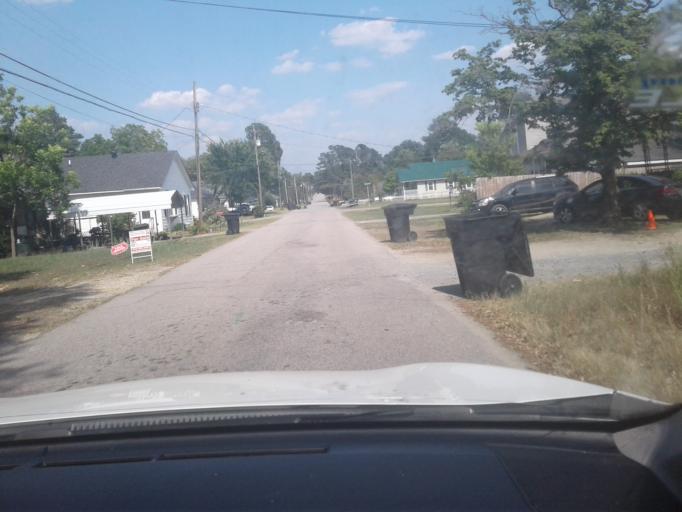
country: US
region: North Carolina
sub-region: Harnett County
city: Erwin
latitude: 35.3239
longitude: -78.6783
